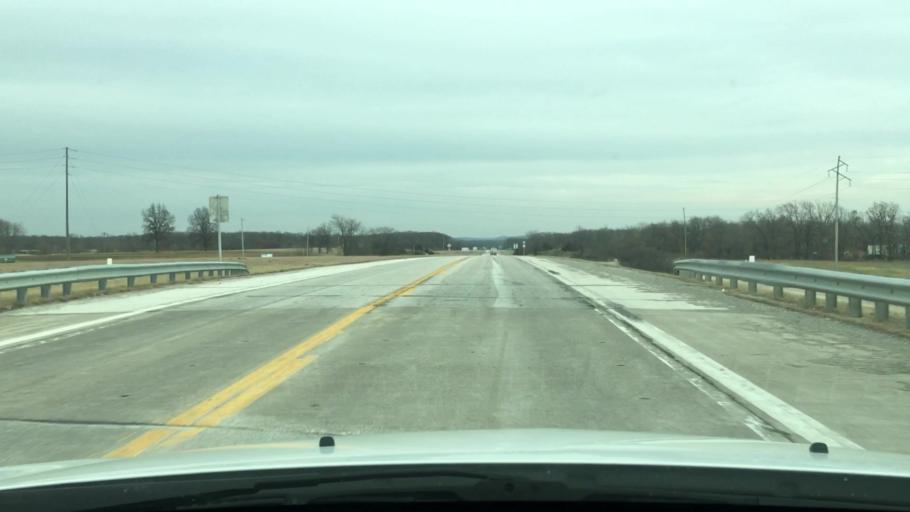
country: US
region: Missouri
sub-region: Pike County
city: Bowling Green
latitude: 39.3560
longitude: -91.2117
